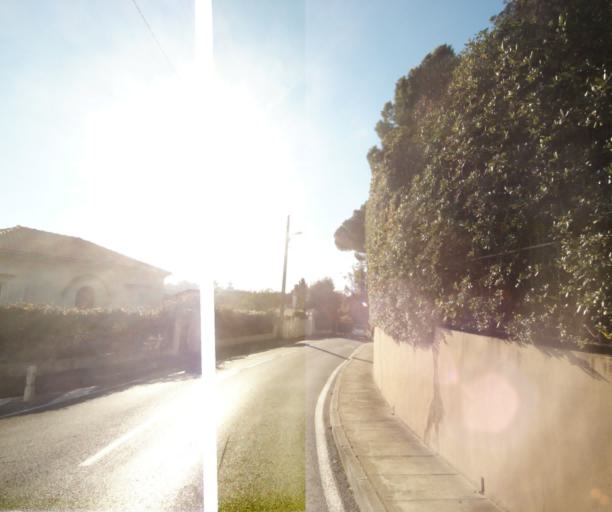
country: FR
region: Provence-Alpes-Cote d'Azur
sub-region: Departement des Alpes-Maritimes
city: Antibes
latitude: 43.5792
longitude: 7.1046
